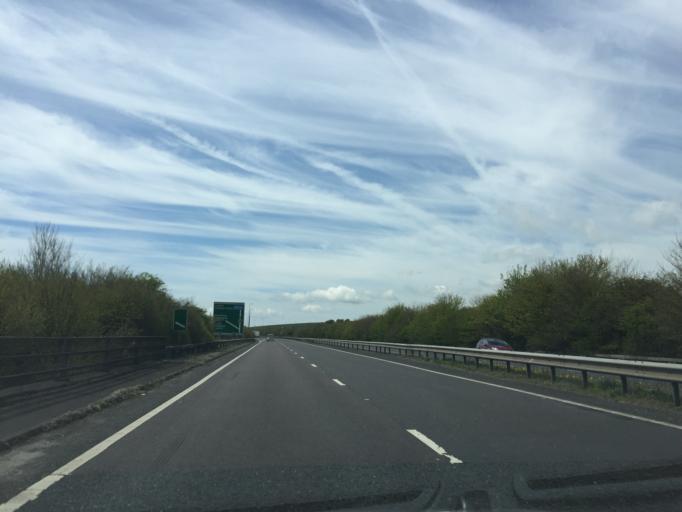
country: GB
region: England
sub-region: Kent
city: Hawkinge
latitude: 51.1101
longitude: 1.1818
